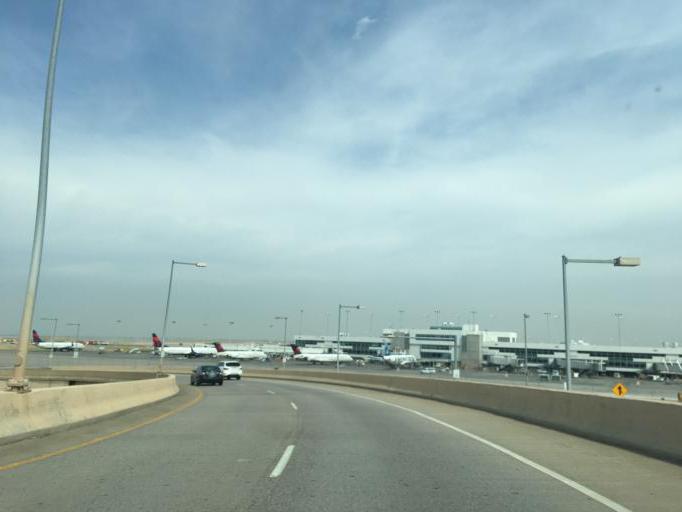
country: US
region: Colorado
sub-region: Weld County
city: Lochbuie
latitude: 39.8510
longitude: -104.6749
